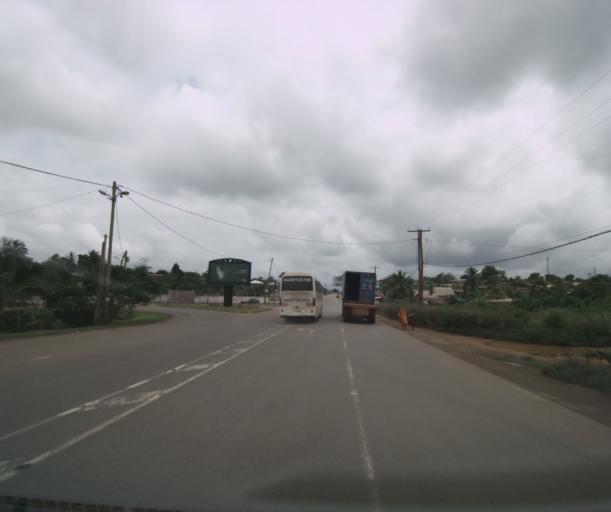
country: CM
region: Littoral
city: Edea
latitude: 3.7888
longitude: 10.1420
